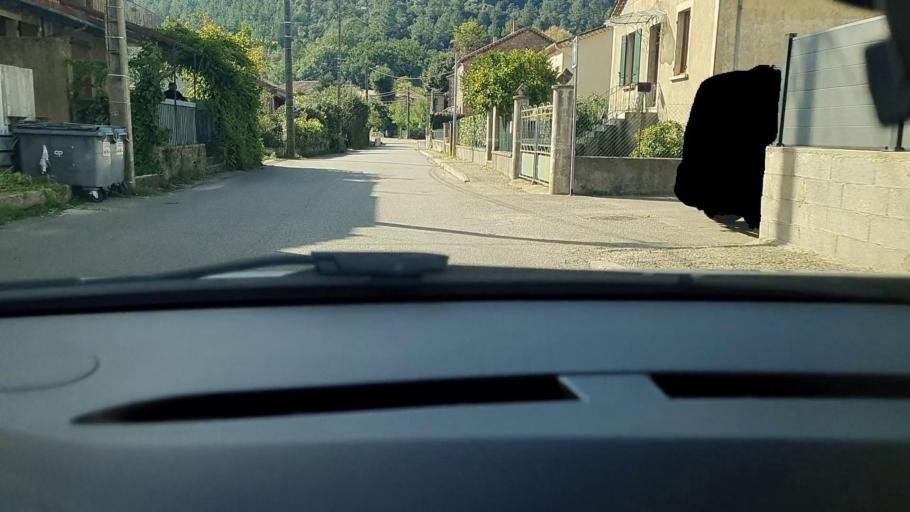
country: FR
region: Languedoc-Roussillon
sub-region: Departement du Gard
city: Molieres-sur-Ceze
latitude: 44.2686
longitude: 4.1492
